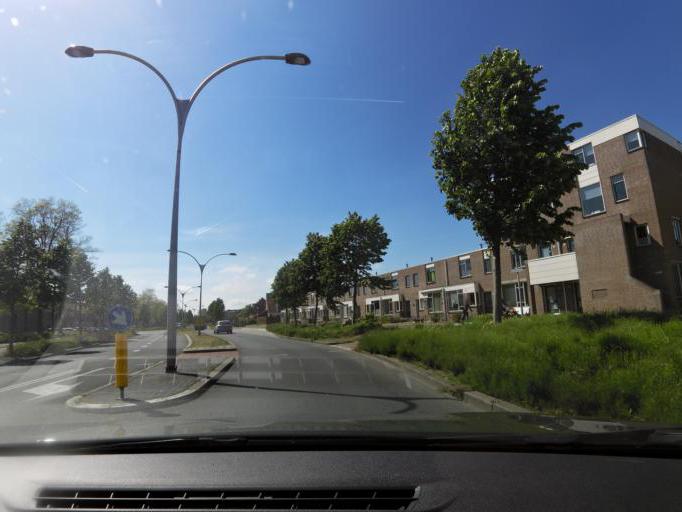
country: NL
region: South Holland
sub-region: Gemeente Hellevoetsluis
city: Hellevoetsluis
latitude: 51.8324
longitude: 4.1565
